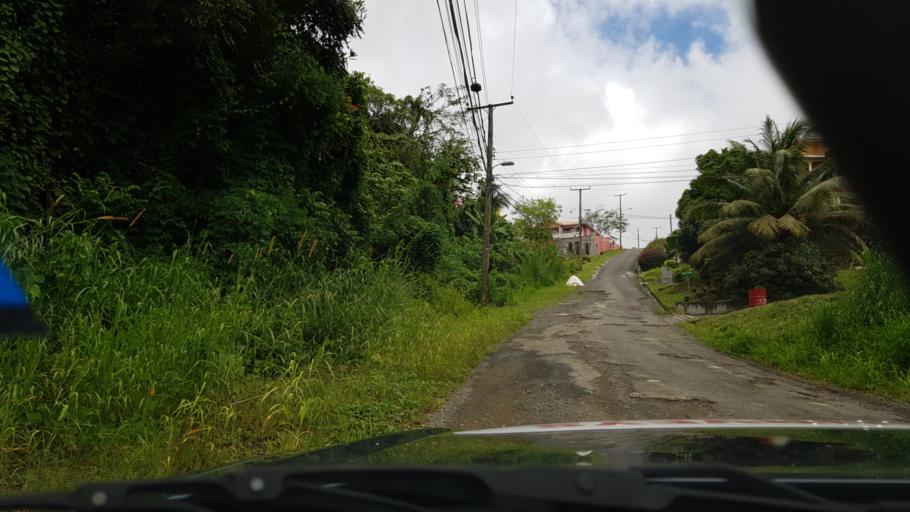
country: LC
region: Anse-la-Raye
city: Anse La Raye
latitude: 13.9494
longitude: -61.0352
